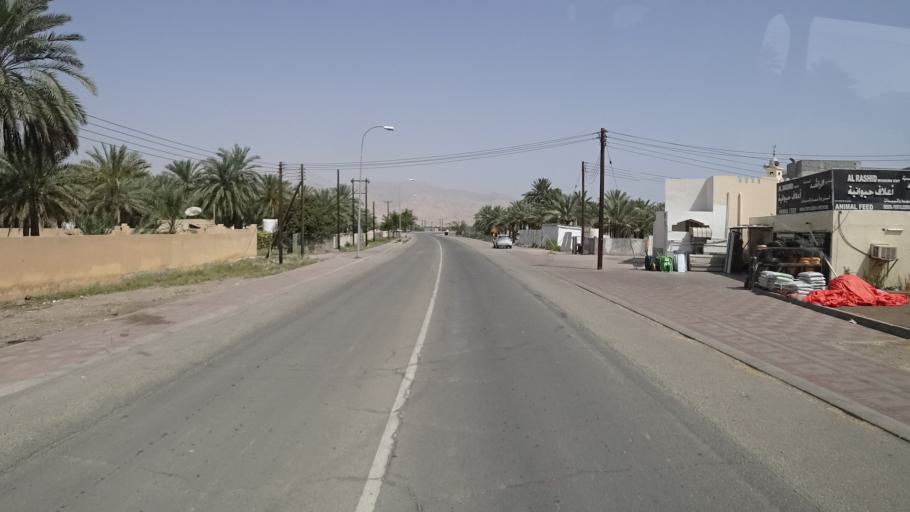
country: OM
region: Muhafazat Masqat
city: Muscat
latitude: 23.2261
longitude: 58.9131
